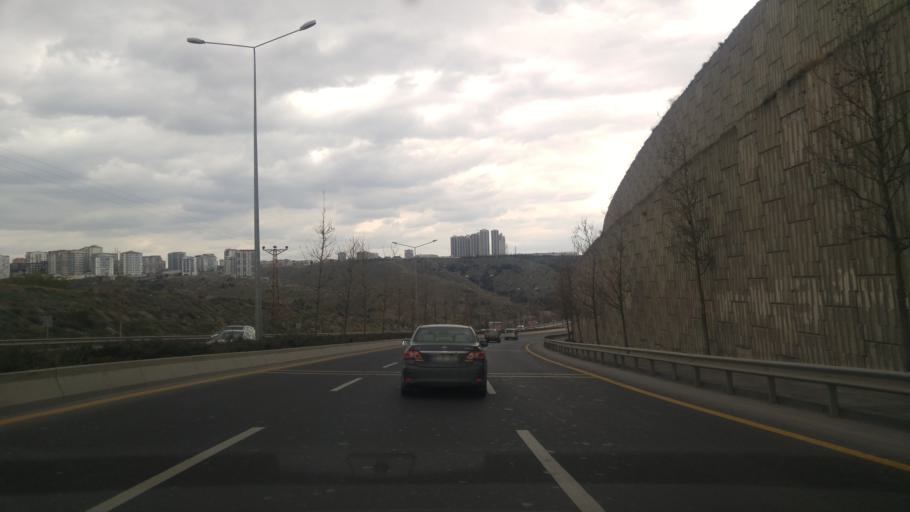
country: TR
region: Ankara
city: Cankaya
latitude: 39.8904
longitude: 32.9012
